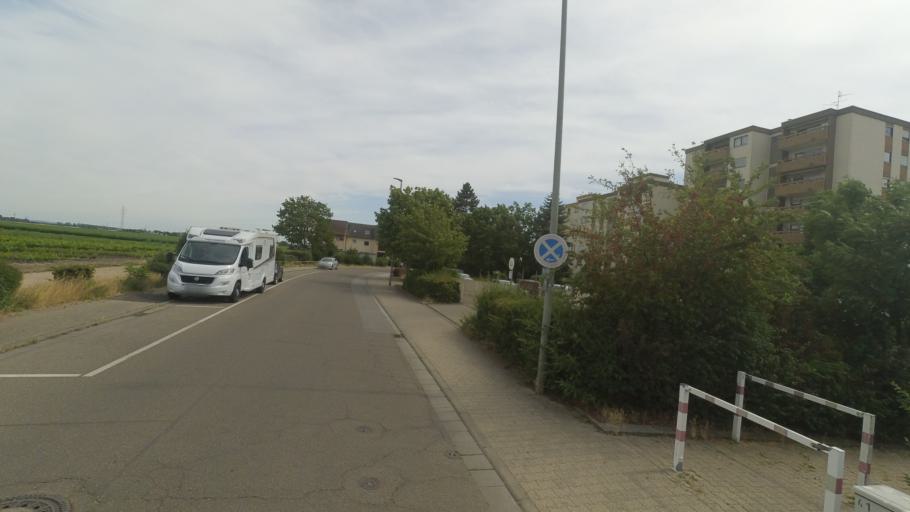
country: DE
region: Rheinland-Pfalz
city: Mutterstadt
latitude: 49.4391
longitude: 8.3692
